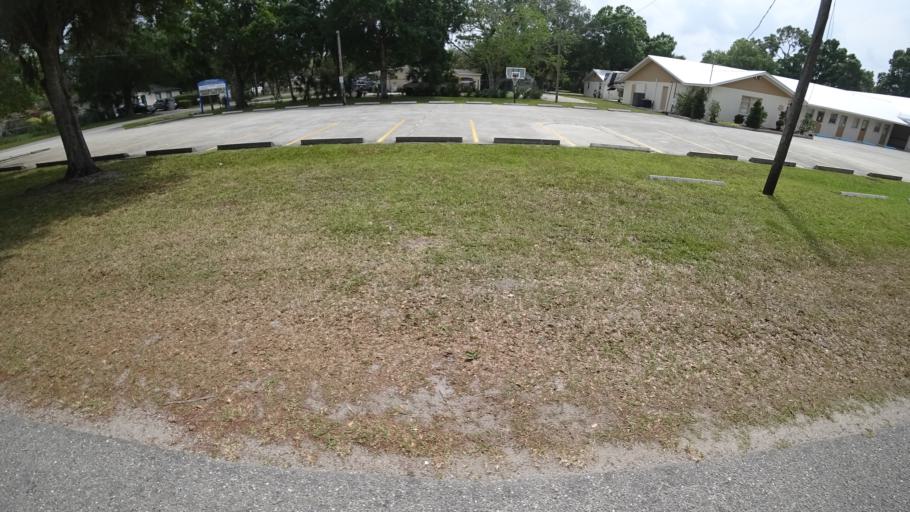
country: US
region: Florida
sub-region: Manatee County
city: Samoset
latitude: 27.4674
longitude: -82.5433
